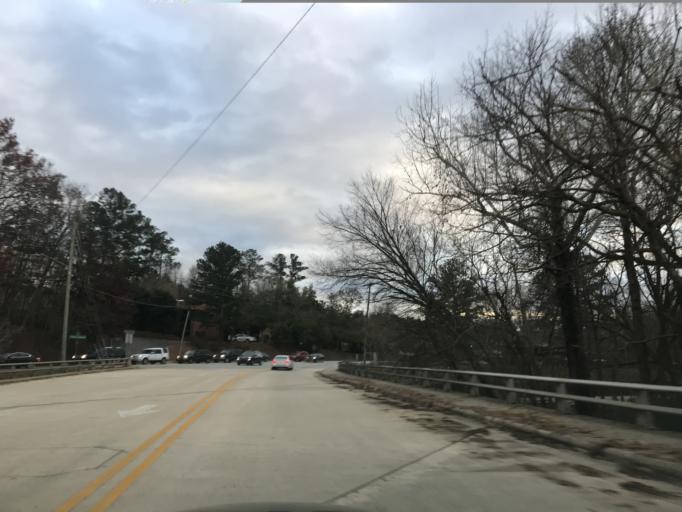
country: US
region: North Carolina
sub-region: Wake County
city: West Raleigh
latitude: 35.8370
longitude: -78.6749
